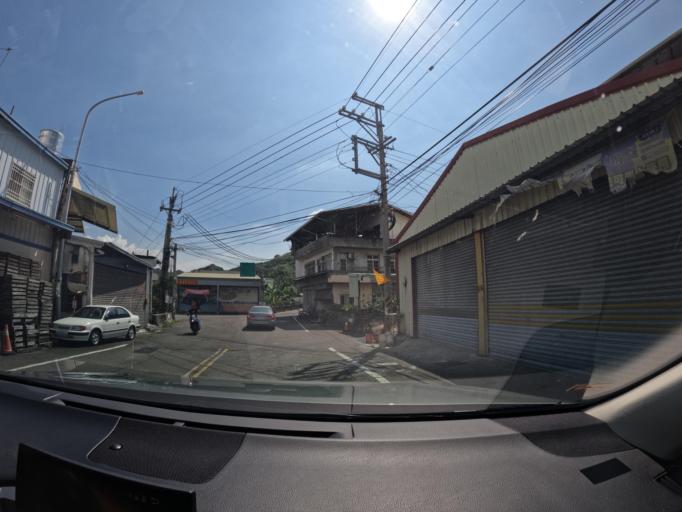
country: TW
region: Taiwan
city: Fengyuan
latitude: 24.3118
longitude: 120.7856
